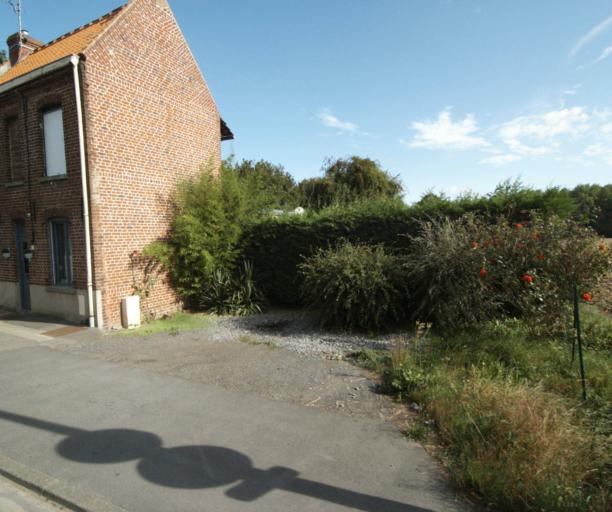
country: FR
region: Nord-Pas-de-Calais
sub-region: Departement du Nord
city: Sainghin-en-Melantois
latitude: 50.5837
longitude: 3.1708
